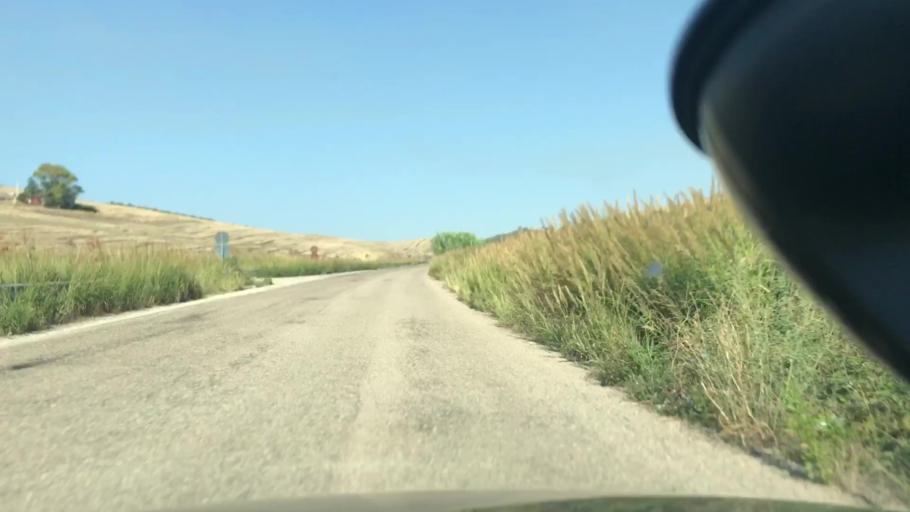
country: IT
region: Basilicate
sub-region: Provincia di Matera
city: Grottole
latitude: 40.6940
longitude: 16.4294
